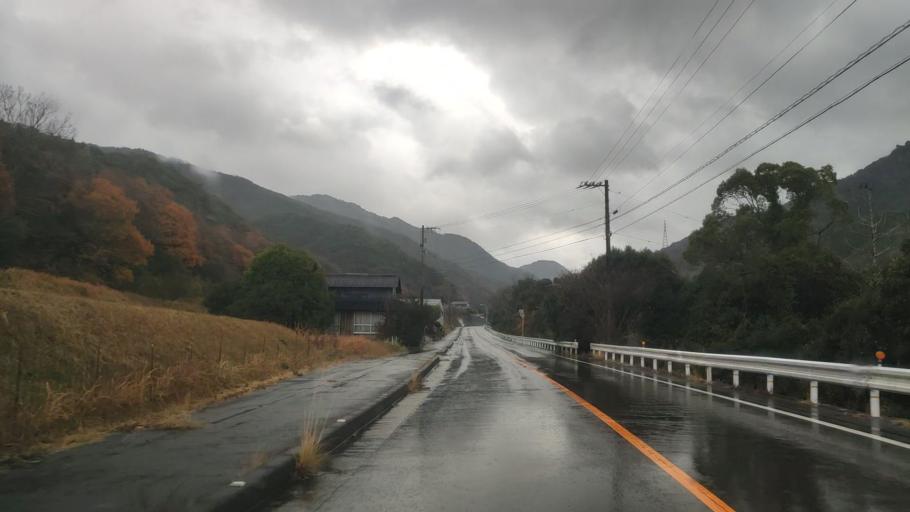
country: JP
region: Tokushima
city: Kamojimacho-jogejima
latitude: 34.1985
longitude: 134.3309
